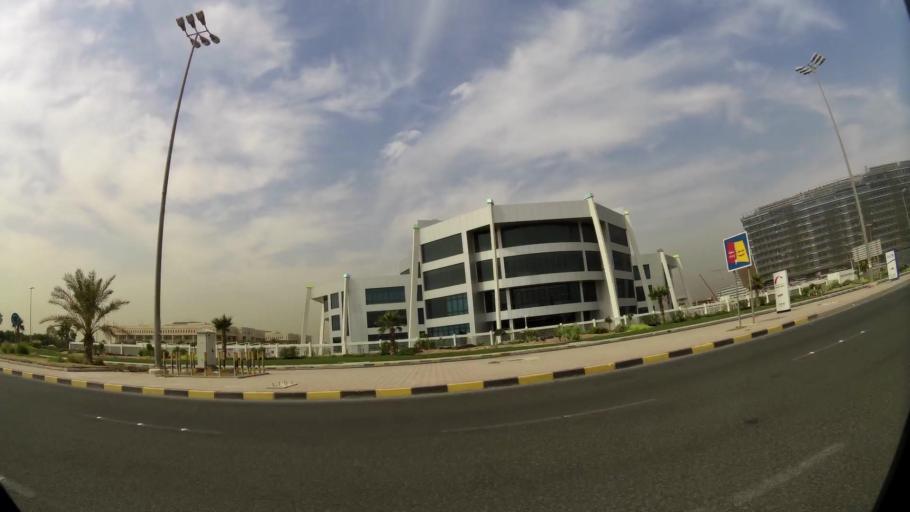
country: KW
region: Mubarak al Kabir
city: Sabah as Salim
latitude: 29.2699
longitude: 48.0226
